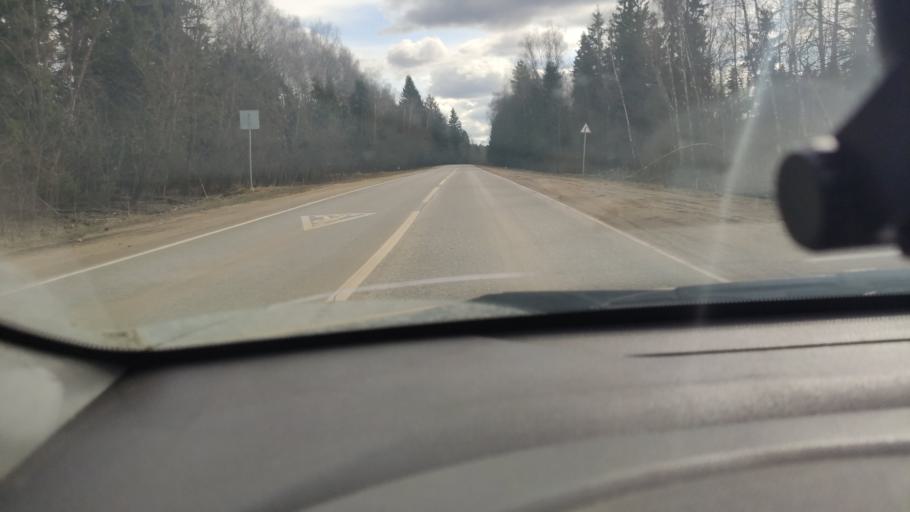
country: RU
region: Moskovskaya
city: Ruza
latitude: 55.7293
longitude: 36.1509
